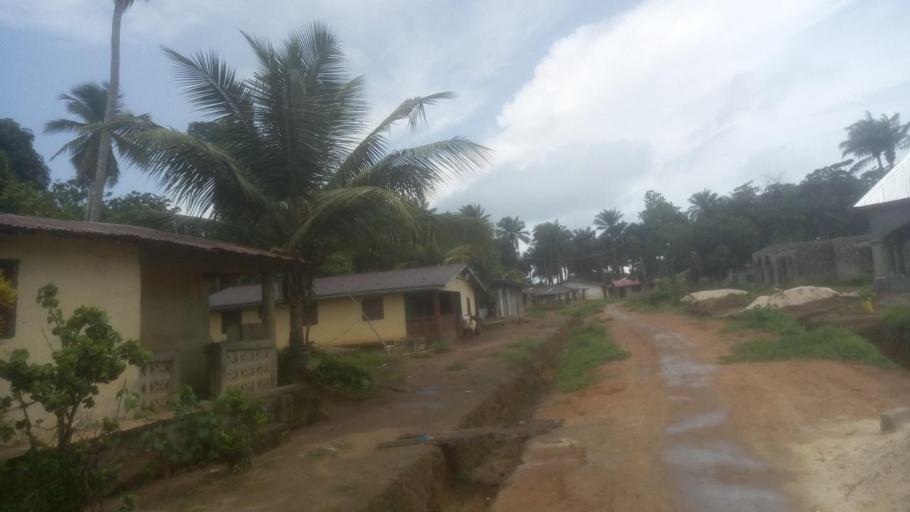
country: SL
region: Northern Province
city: Tintafor
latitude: 8.6395
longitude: -13.2190
